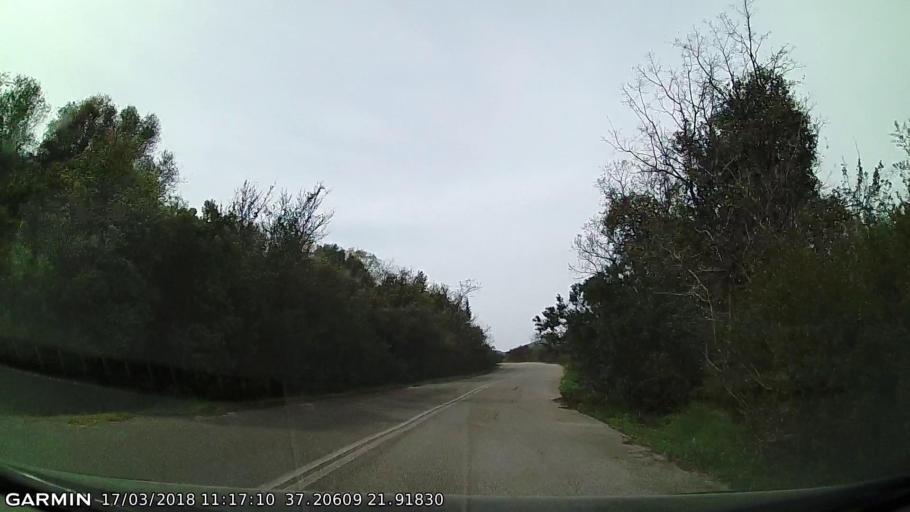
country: GR
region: Peloponnese
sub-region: Nomos Messinias
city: Meligalas
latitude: 37.2060
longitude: 21.9182
